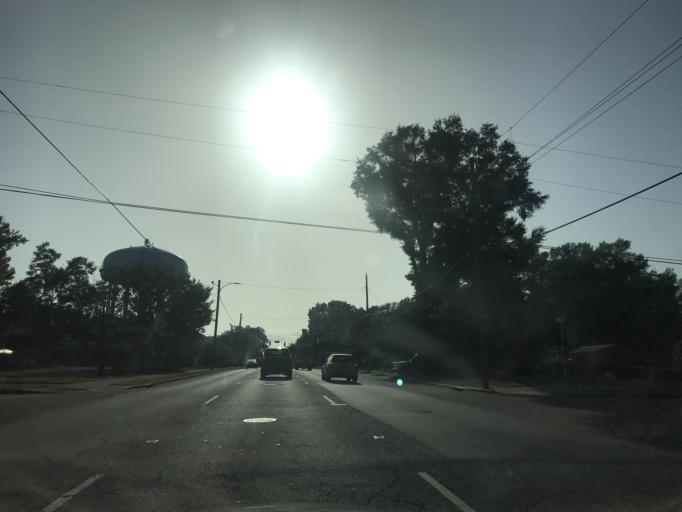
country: US
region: North Carolina
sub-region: New Hanover County
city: Wilmington
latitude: 34.2263
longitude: -77.9340
